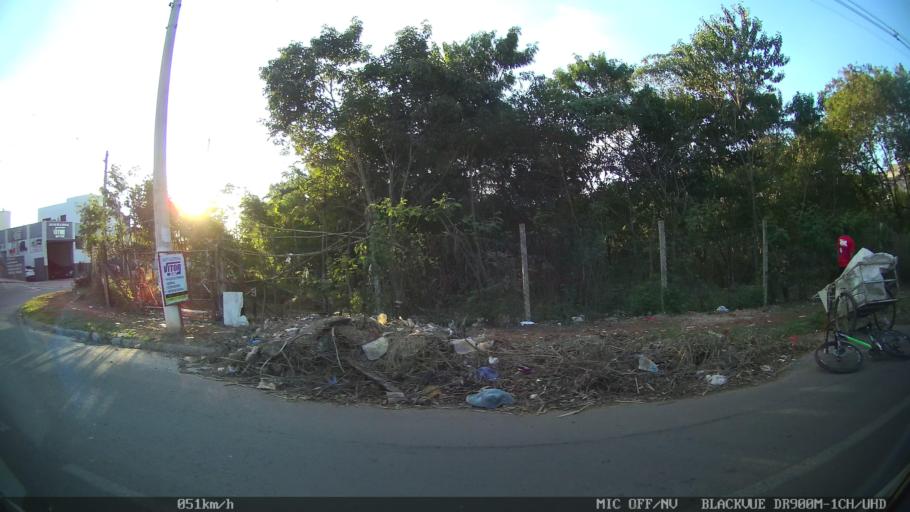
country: BR
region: Sao Paulo
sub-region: Santa Barbara D'Oeste
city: Santa Barbara d'Oeste
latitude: -22.7354
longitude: -47.3932
